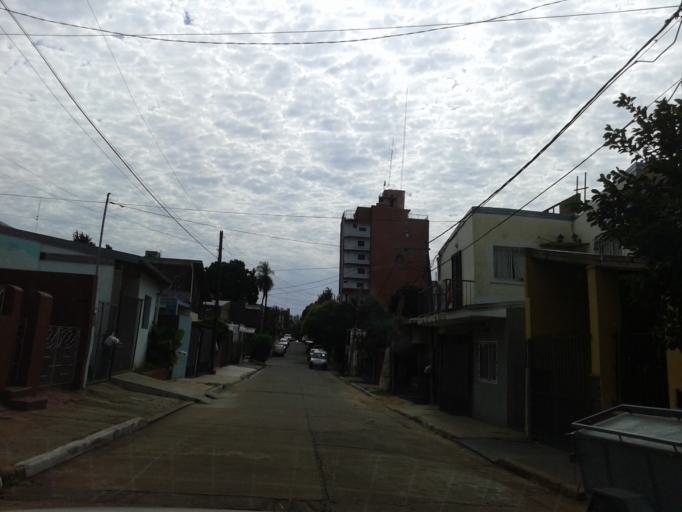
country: AR
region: Misiones
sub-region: Departamento de Capital
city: Posadas
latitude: -27.3772
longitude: -55.8929
